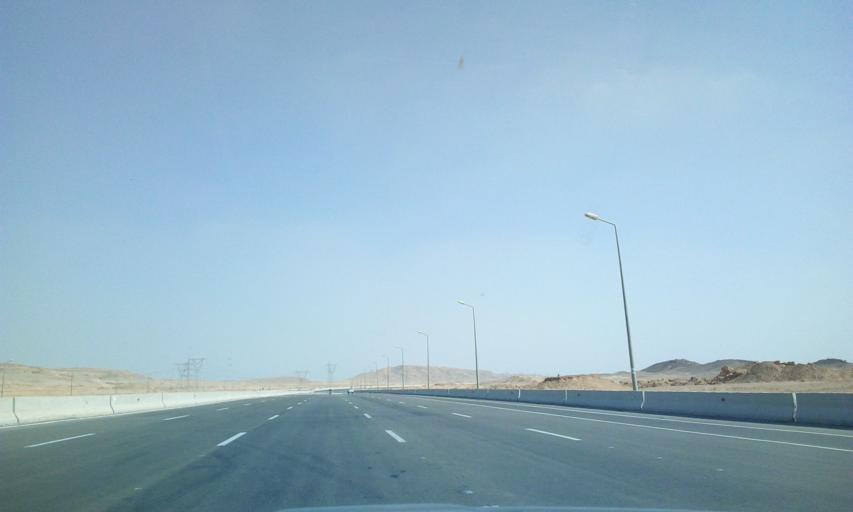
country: EG
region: As Suways
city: Ain Sukhna
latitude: 29.8659
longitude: 31.8612
